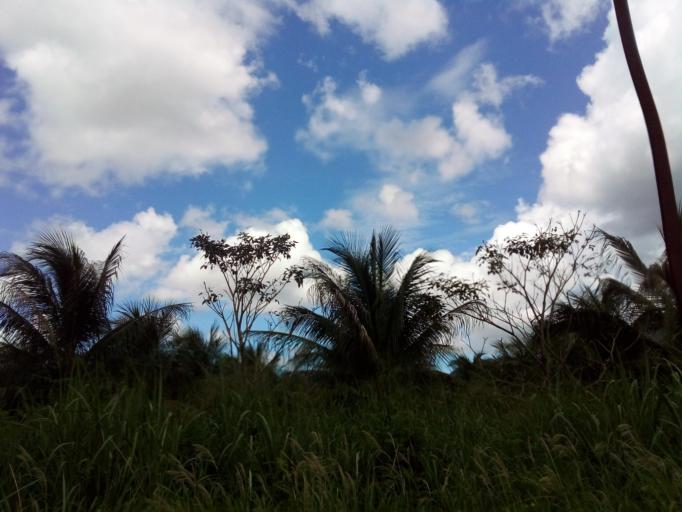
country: BR
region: Espirito Santo
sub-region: Ibiracu
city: Ibiracu
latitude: -19.8792
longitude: -40.3624
